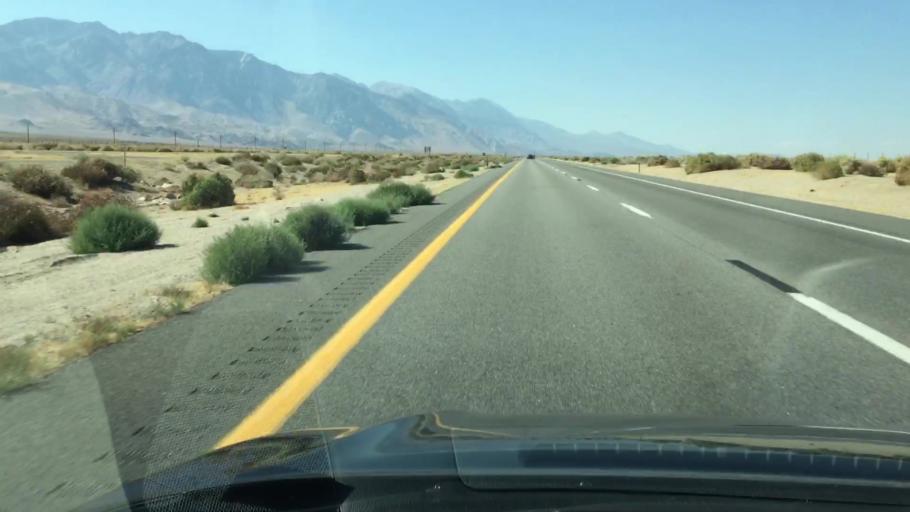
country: US
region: California
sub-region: Inyo County
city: Lone Pine
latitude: 36.7615
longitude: -118.1696
